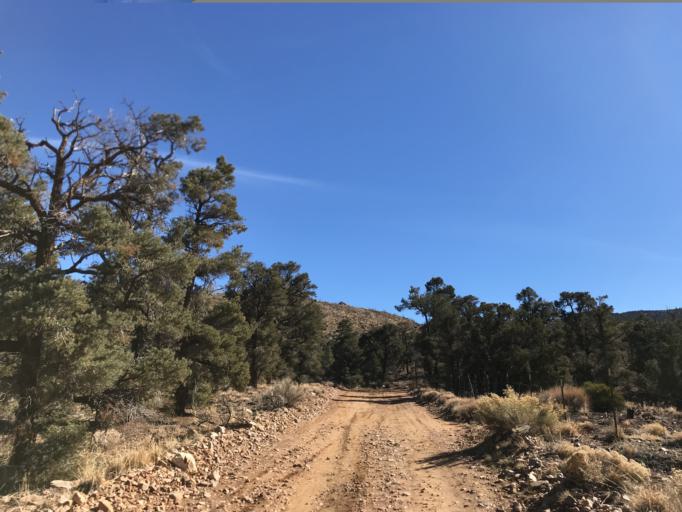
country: US
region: California
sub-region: San Bernardino County
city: Big Bear City
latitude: 34.2551
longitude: -116.7405
